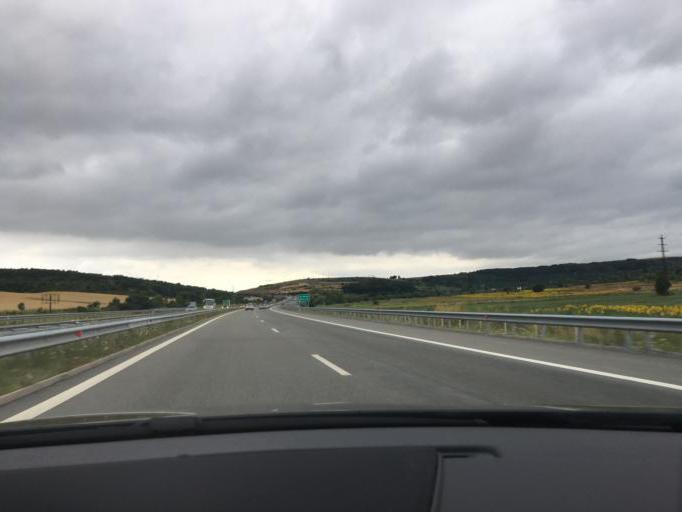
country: BG
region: Kyustendil
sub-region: Obshtina Bobovdol
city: Bobovdol
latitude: 42.3932
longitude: 23.1193
